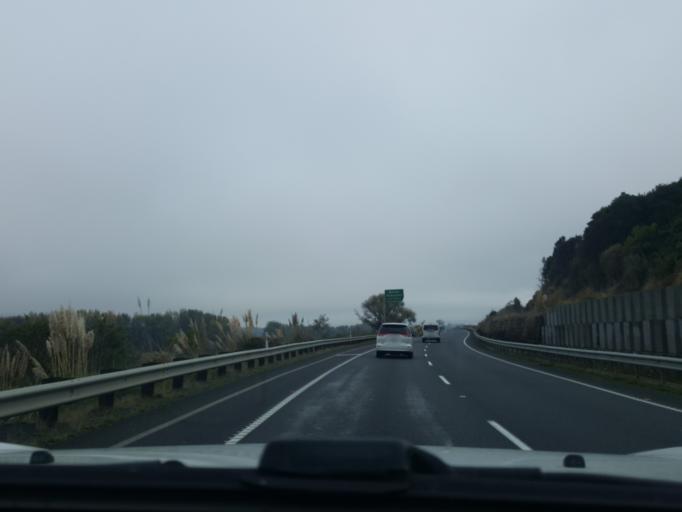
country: NZ
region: Waikato
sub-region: Waikato District
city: Te Kauwhata
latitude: -37.2923
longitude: 175.0578
